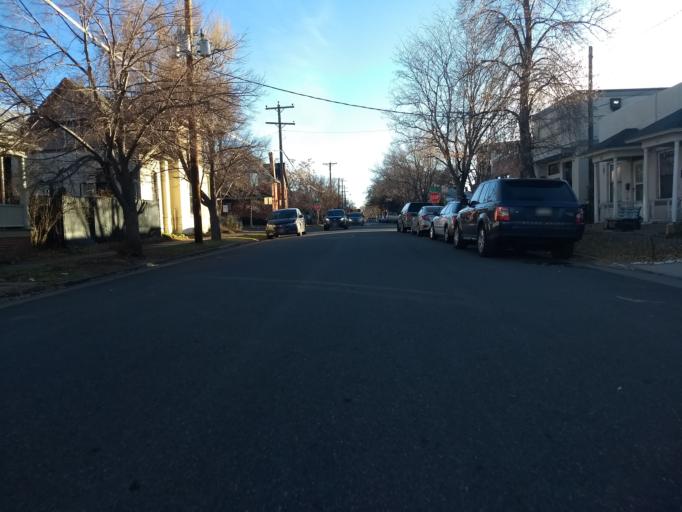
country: US
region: Colorado
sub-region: Denver County
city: Denver
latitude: 39.7189
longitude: -104.9922
